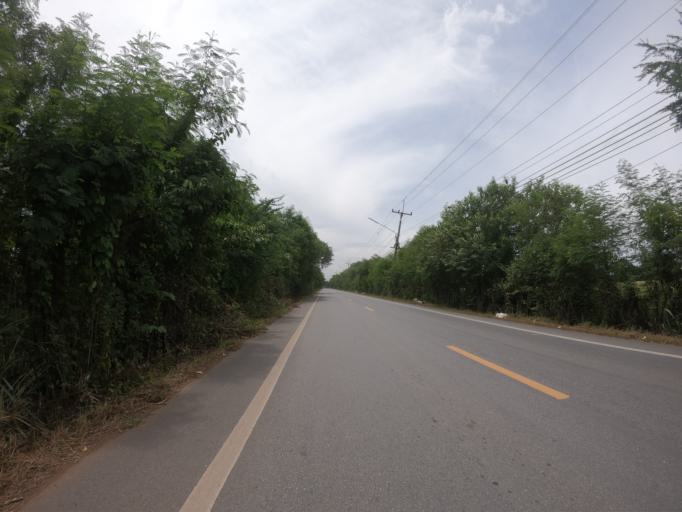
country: TH
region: Pathum Thani
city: Nong Suea
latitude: 14.0637
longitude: 100.8716
